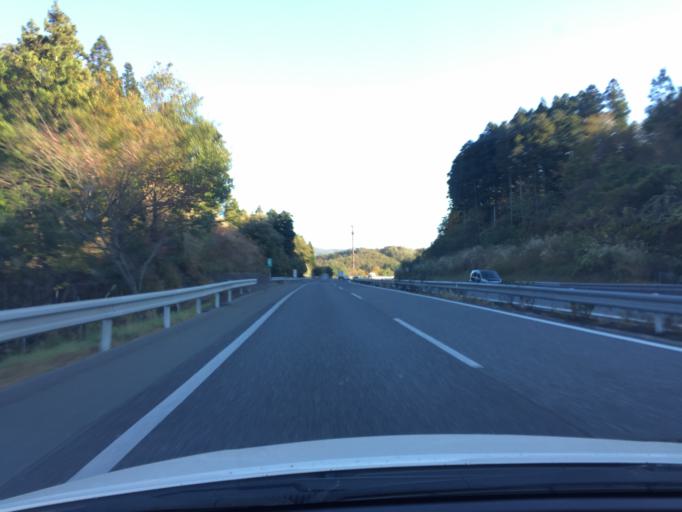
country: JP
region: Fukushima
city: Iwaki
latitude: 37.1442
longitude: 140.7452
